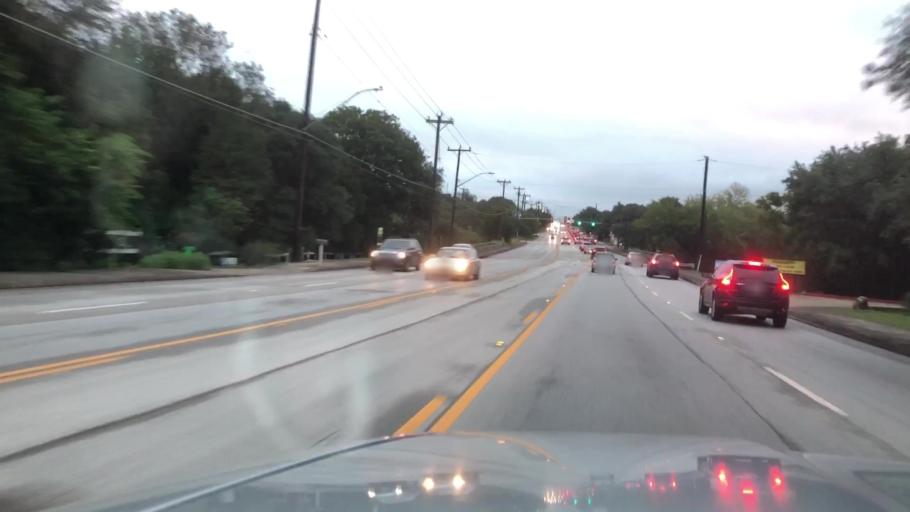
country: US
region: Texas
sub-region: Bexar County
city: Leon Valley
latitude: 29.5356
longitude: -98.6076
